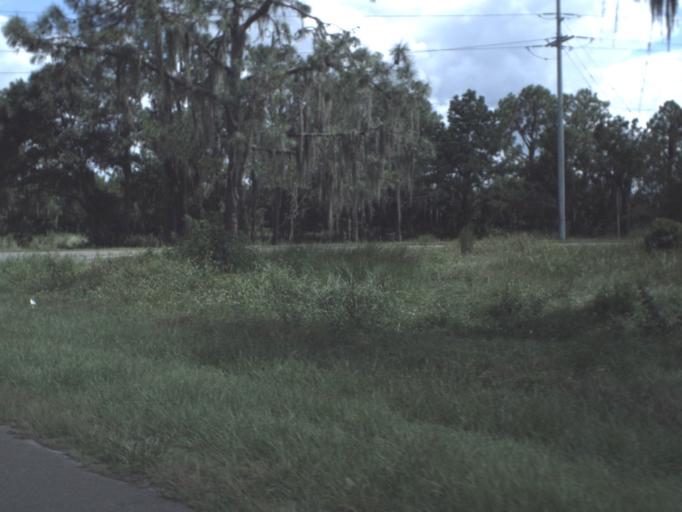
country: US
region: Florida
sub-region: Polk County
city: Mulberry
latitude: 27.7047
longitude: -82.0208
